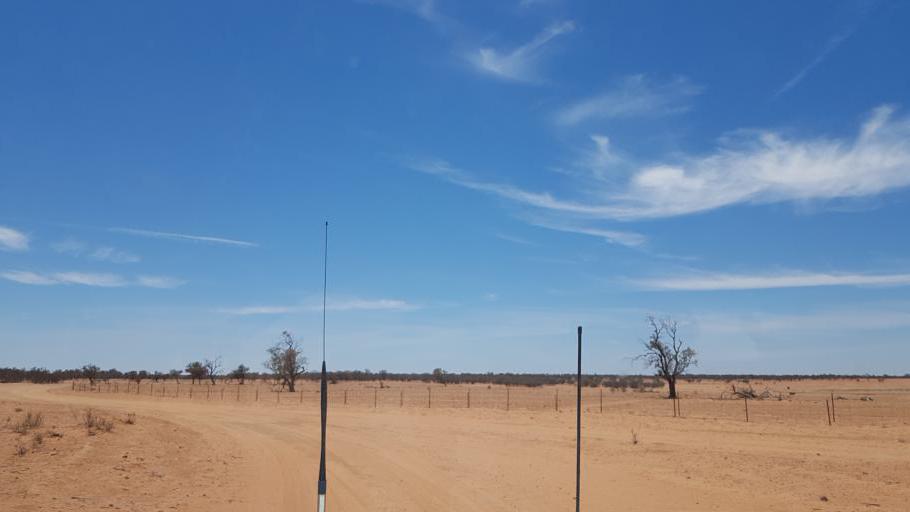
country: AU
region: New South Wales
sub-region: Wentworth
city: Dareton
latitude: -33.3472
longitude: 141.4550
